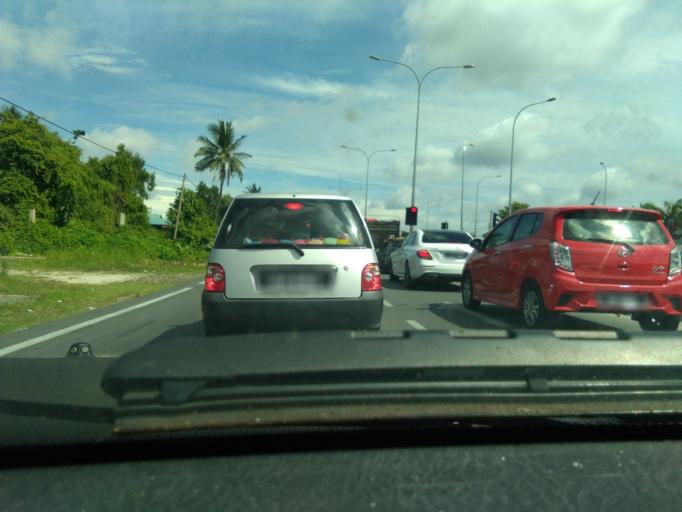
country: MY
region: Perak
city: Parit Buntar
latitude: 5.1006
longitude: 100.4877
